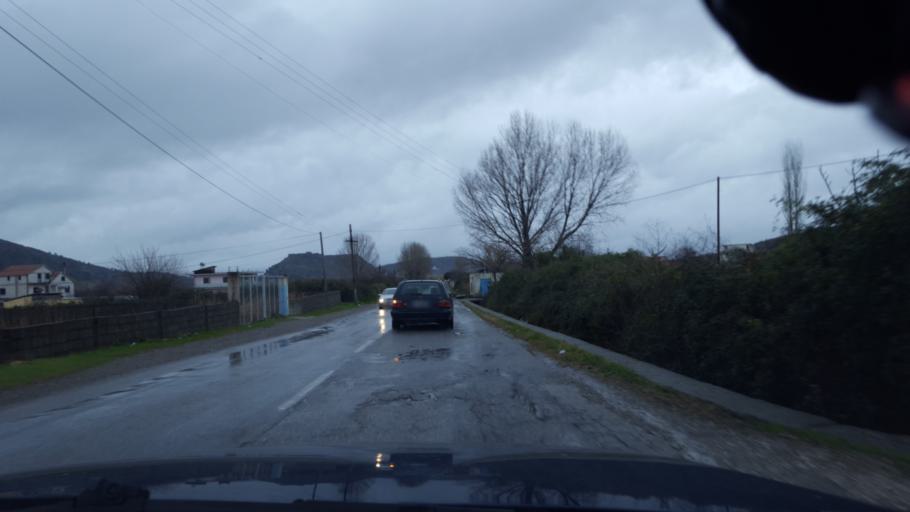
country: AL
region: Shkoder
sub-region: Rrethi i Shkodres
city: Berdica e Madhe
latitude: 42.0231
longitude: 19.4865
